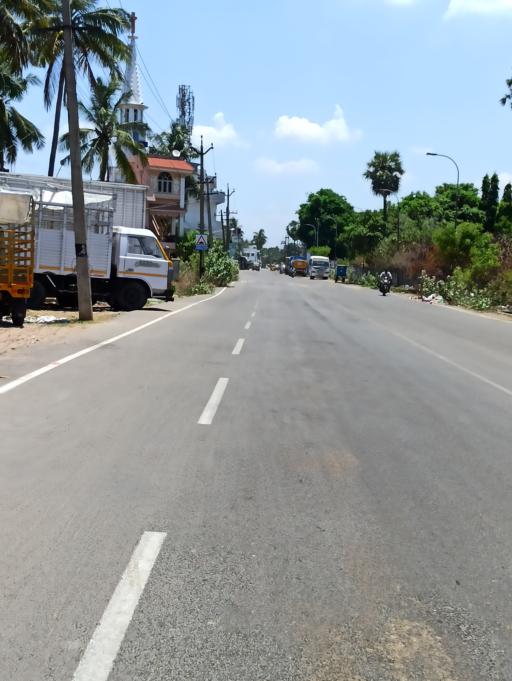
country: IN
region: Tamil Nadu
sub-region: Thiruvallur
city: Chinnasekkadu
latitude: 13.1537
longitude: 80.2409
